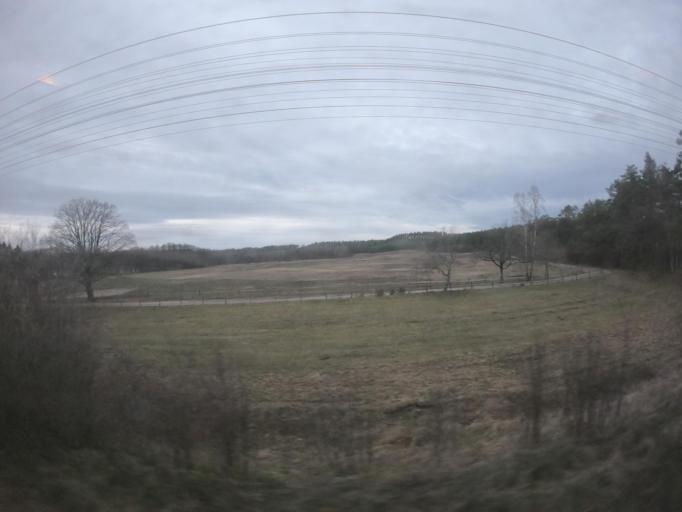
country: PL
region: West Pomeranian Voivodeship
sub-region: Powiat szczecinecki
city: Lubowo
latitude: 53.5997
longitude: 16.4293
